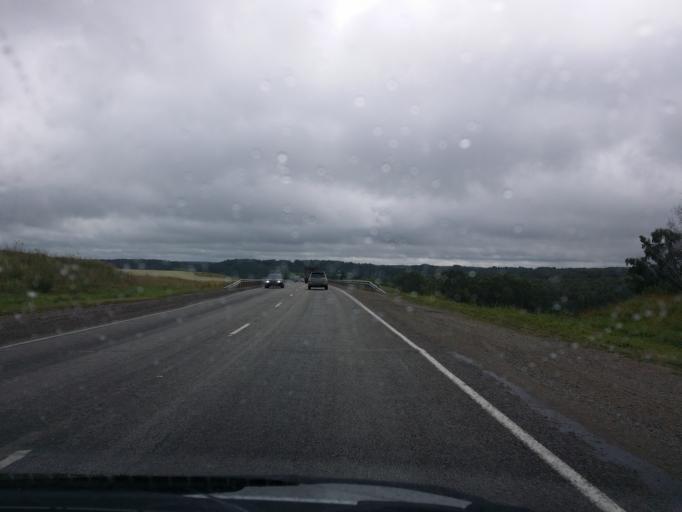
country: RU
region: Altai Krai
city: Nalobikha
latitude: 53.1585
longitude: 84.6729
